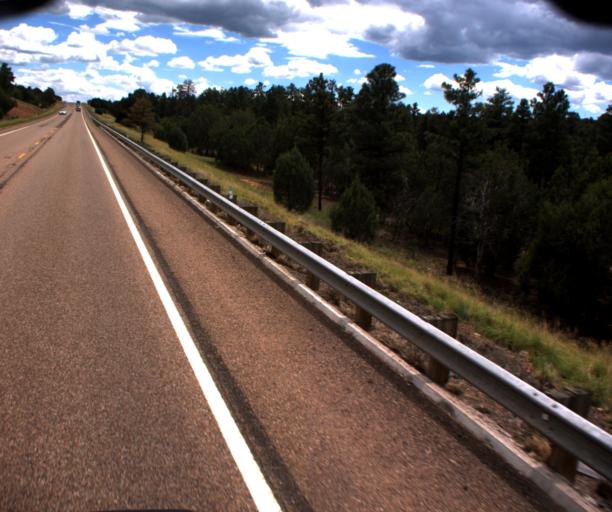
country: US
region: Arizona
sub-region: Navajo County
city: Linden
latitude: 34.2998
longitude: -110.1957
